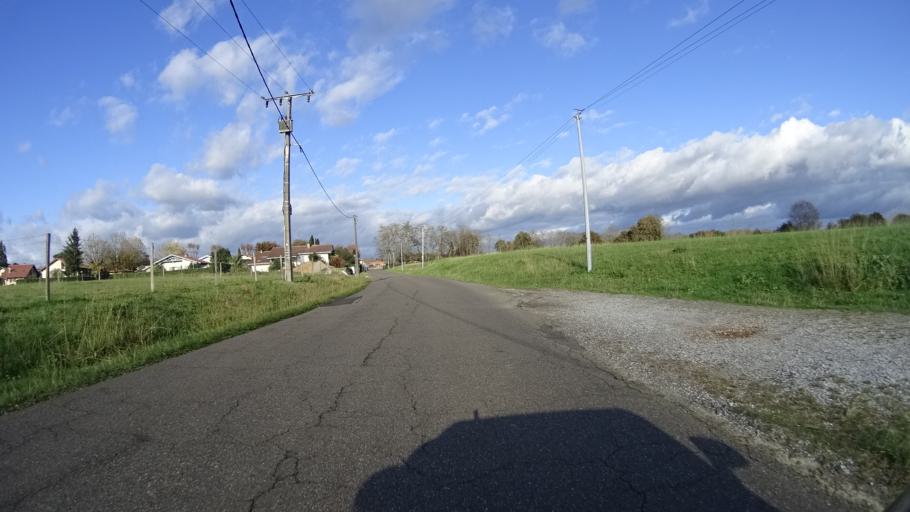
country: FR
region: Aquitaine
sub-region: Departement des Landes
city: Mees
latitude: 43.7202
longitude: -1.0844
